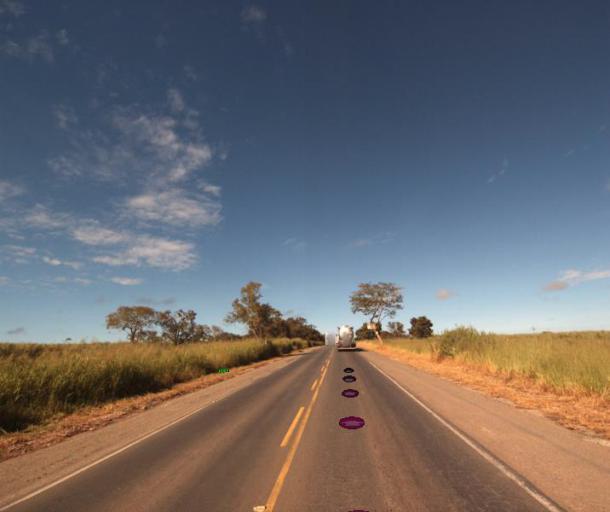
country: BR
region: Goias
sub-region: Itapaci
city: Itapaci
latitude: -14.8312
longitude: -49.3045
